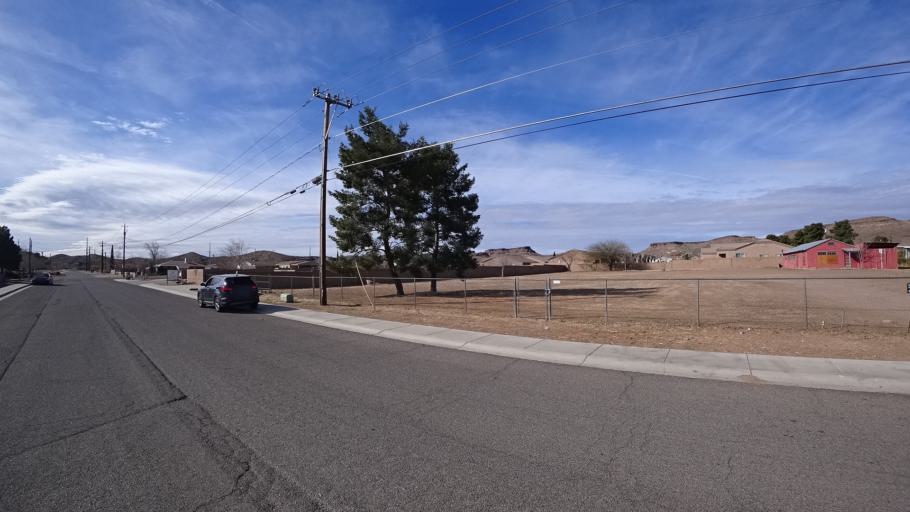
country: US
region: Arizona
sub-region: Mohave County
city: Kingman
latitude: 35.2199
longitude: -114.0446
